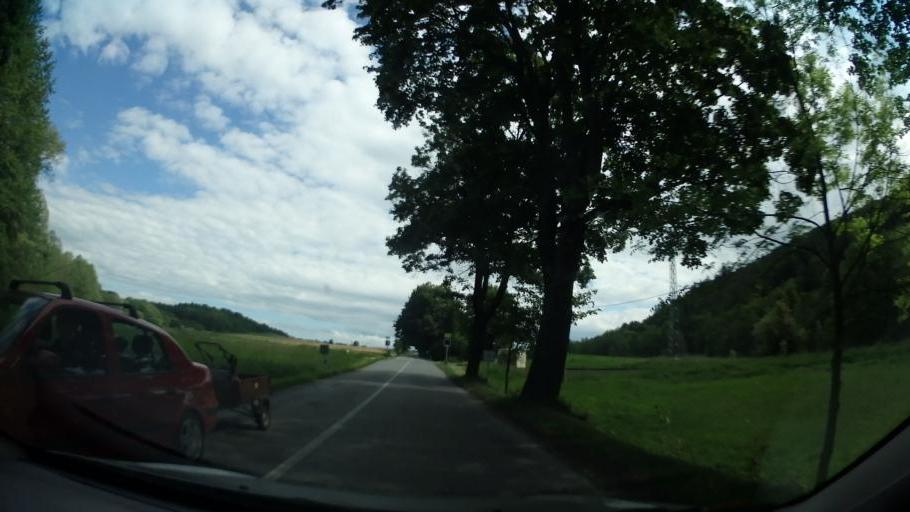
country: CZ
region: Pardubicky
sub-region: Okres Svitavy
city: Moravska Trebova
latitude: 49.7777
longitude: 16.6652
